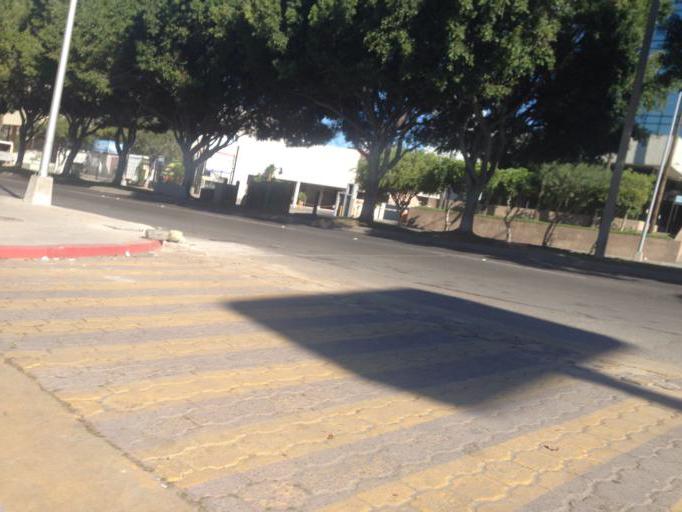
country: MX
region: Baja California
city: Tijuana
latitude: 32.5308
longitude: -117.0153
